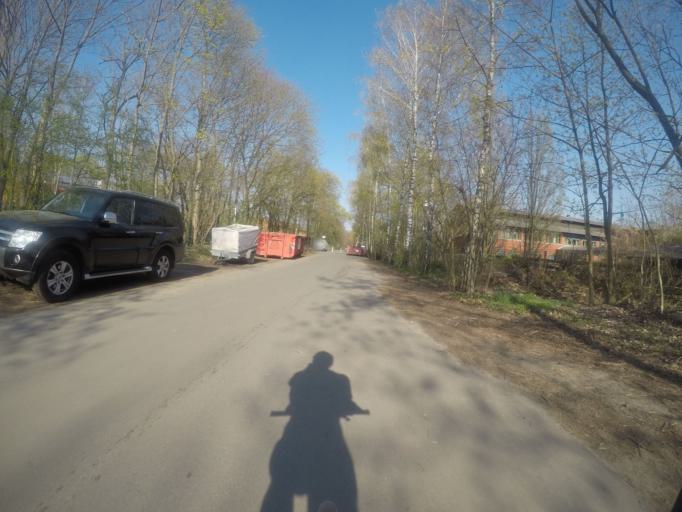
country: DE
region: Berlin
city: Zehlendorf Bezirk
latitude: 52.4280
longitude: 13.2359
